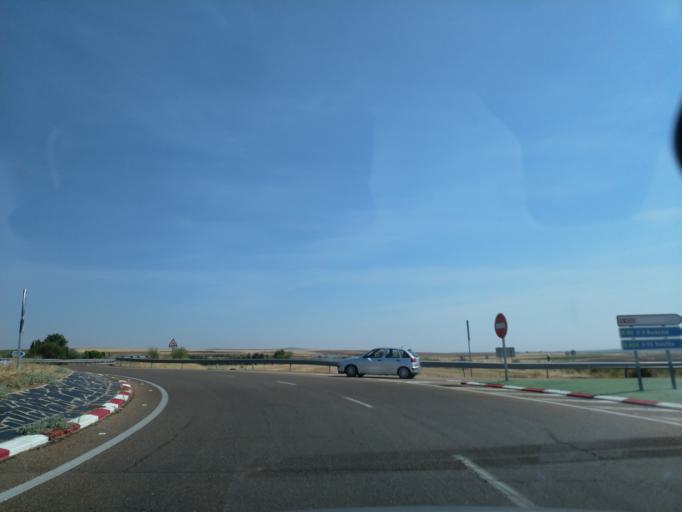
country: ES
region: Extremadura
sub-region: Provincia de Badajoz
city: Merida
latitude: 38.9399
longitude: -6.3433
